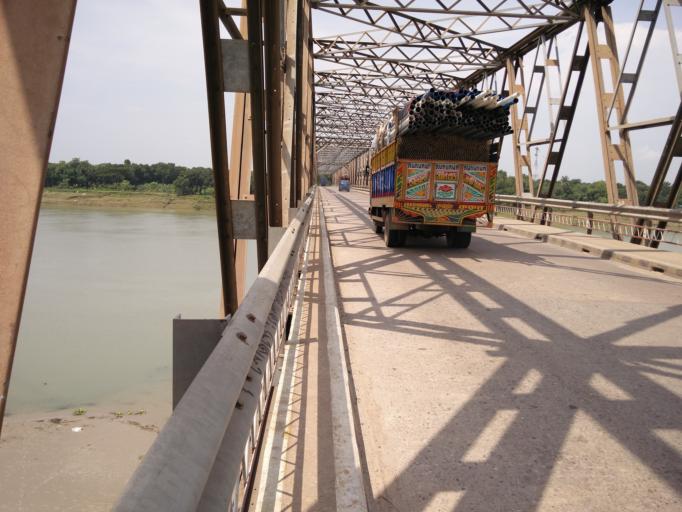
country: BD
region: Khulna
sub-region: Magura
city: Magura
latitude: 23.5428
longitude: 89.5175
